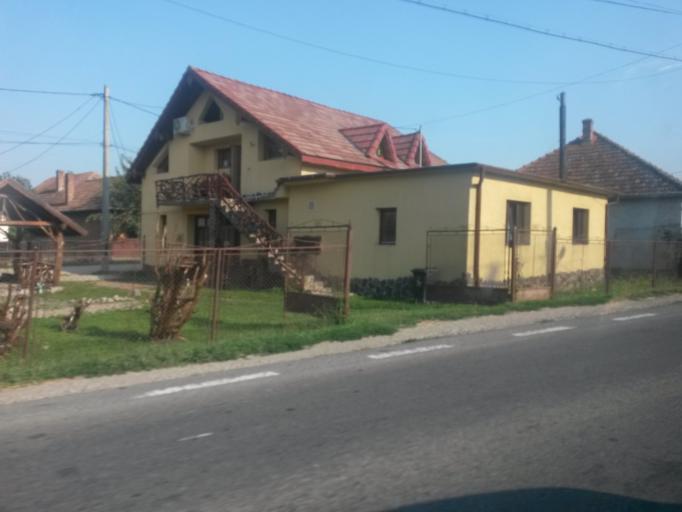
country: RO
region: Alba
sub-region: Comuna Unirea
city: Unirea
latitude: 46.3978
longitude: 23.8090
